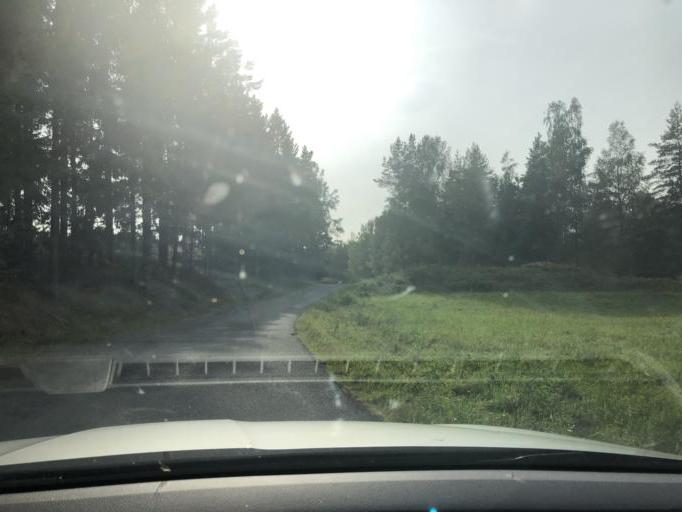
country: SE
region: Joenkoeping
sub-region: Vetlanda Kommun
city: Ekenassjon
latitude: 57.4941
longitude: 14.8988
